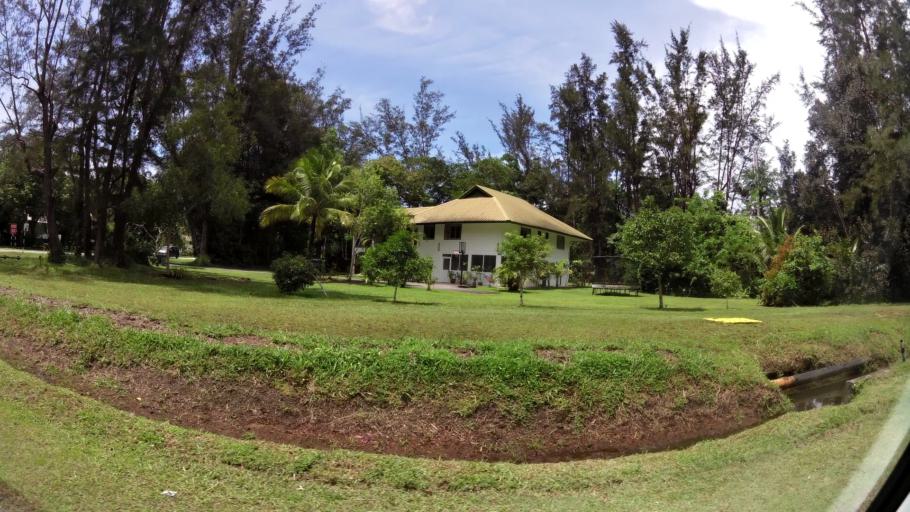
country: BN
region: Belait
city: Seria
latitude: 4.6043
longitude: 114.2845
